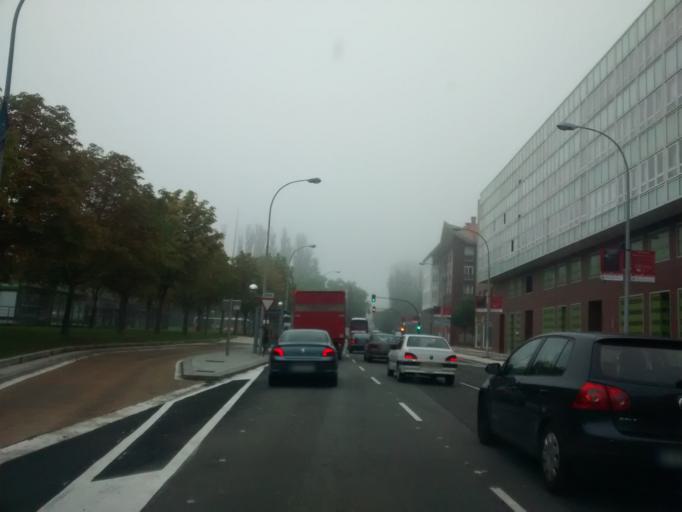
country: ES
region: Basque Country
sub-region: Provincia de Alava
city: Gasteiz / Vitoria
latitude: 42.8606
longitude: -2.6834
